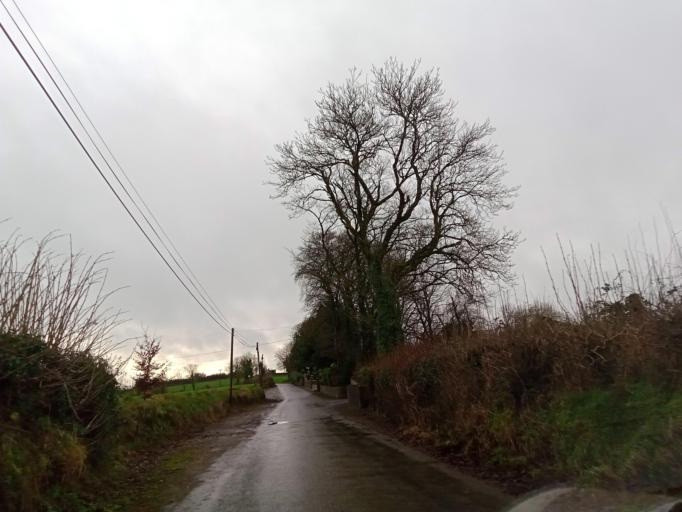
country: IE
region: Munster
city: Fethard
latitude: 52.5588
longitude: -7.6956
